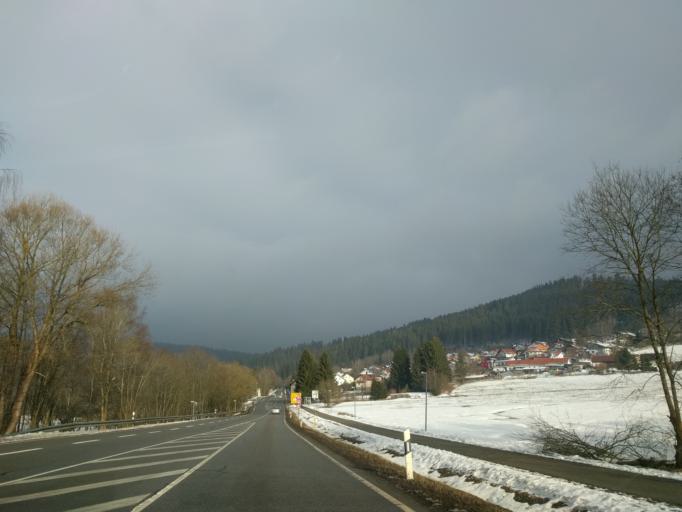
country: DE
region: Bavaria
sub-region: Lower Bavaria
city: Zwiesel
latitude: 49.0335
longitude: 13.2348
